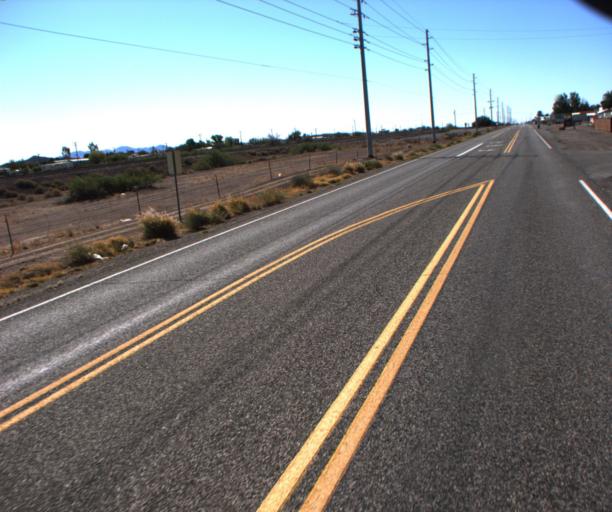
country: US
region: Arizona
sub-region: La Paz County
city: Cienega Springs
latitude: 33.9352
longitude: -114.0080
